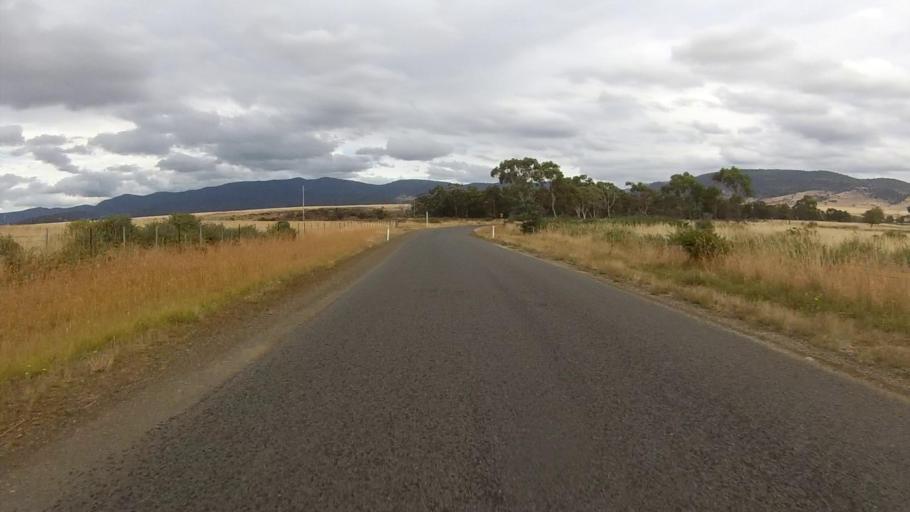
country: AU
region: Tasmania
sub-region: Northern Midlands
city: Evandale
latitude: -41.8124
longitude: 147.7536
